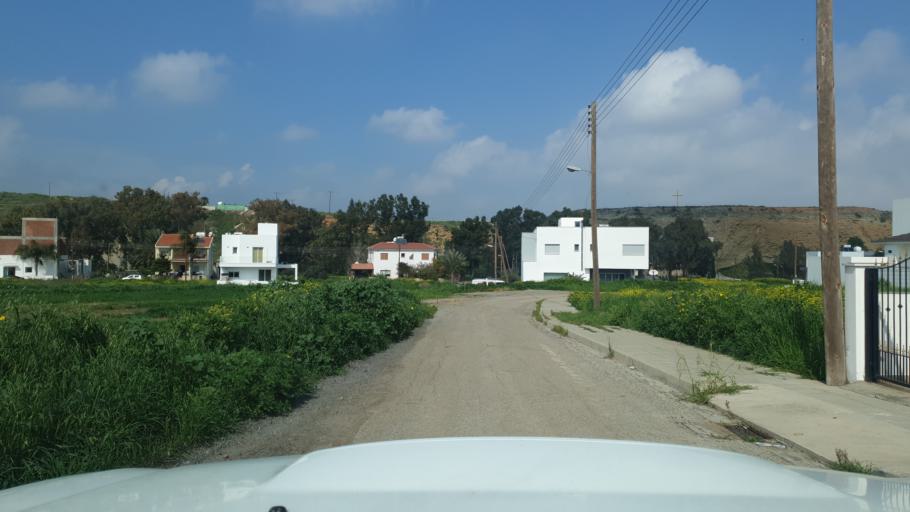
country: CY
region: Lefkosia
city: Kato Deftera
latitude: 35.0891
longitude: 33.2817
